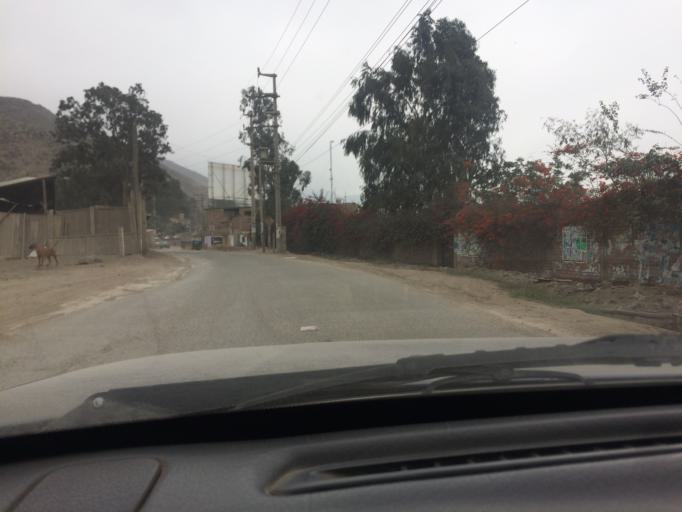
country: PE
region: Lima
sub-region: Lima
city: Cieneguilla
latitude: -12.1730
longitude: -76.8616
